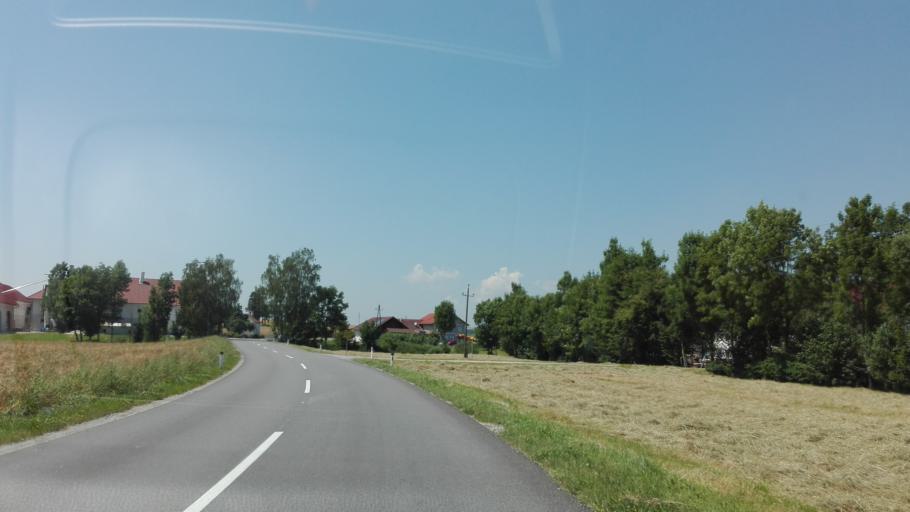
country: AT
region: Upper Austria
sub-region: Politischer Bezirk Grieskirchen
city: Grieskirchen
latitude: 48.3457
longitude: 13.8707
